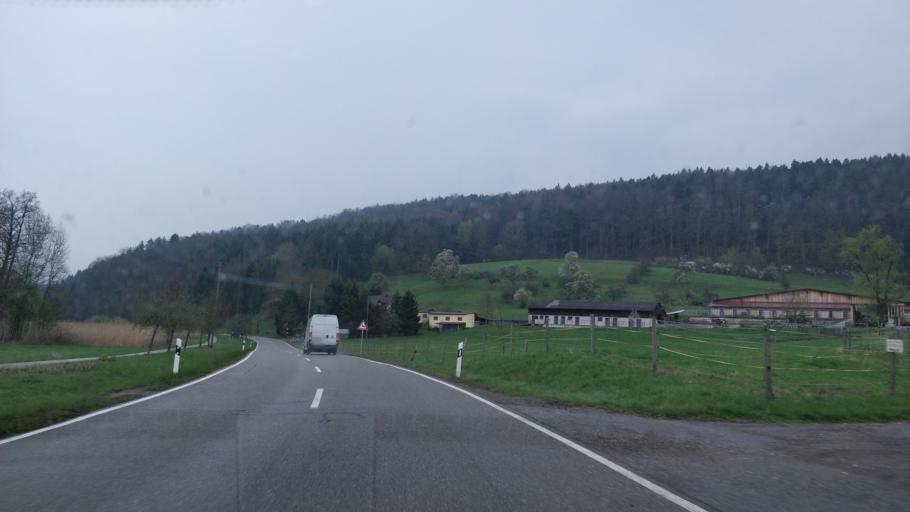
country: DE
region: Baden-Wuerttemberg
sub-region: Regierungsbezirk Stuttgart
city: Oberrot
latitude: 49.0221
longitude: 9.6600
